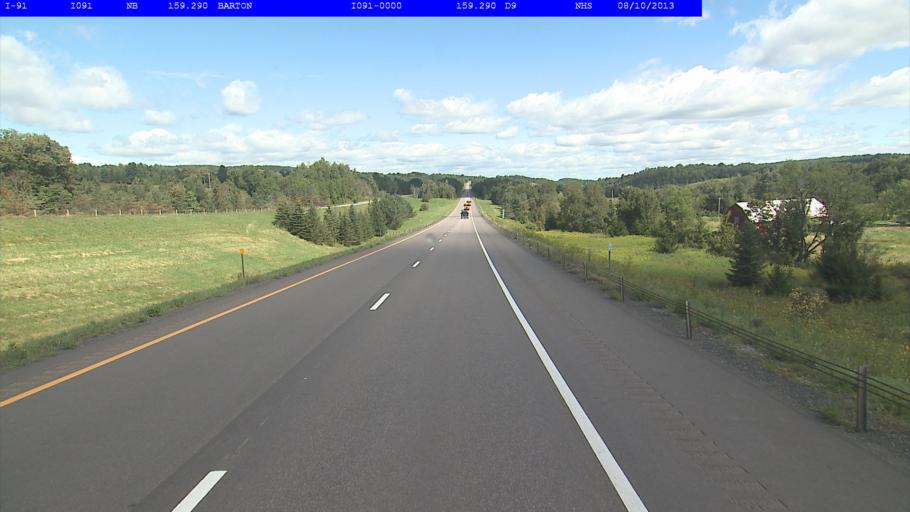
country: US
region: Vermont
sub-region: Orleans County
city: Newport
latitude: 44.7761
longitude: -72.2147
